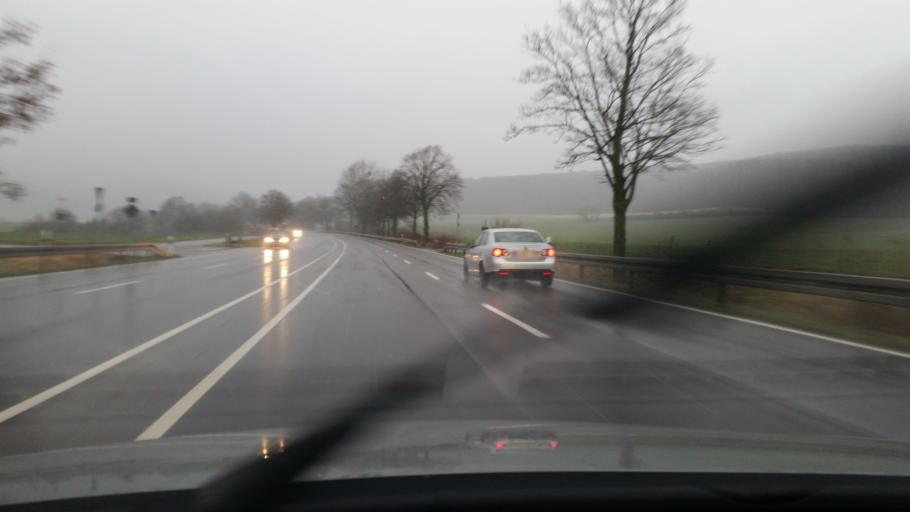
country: DE
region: Lower Saxony
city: Springe
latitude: 52.1880
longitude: 9.5287
